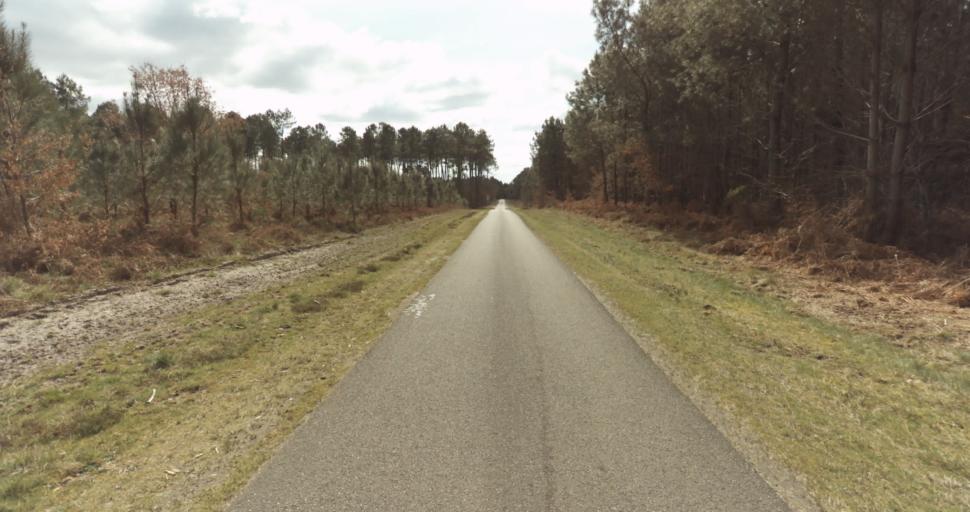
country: FR
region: Aquitaine
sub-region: Departement des Landes
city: Roquefort
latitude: 44.0514
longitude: -0.4264
